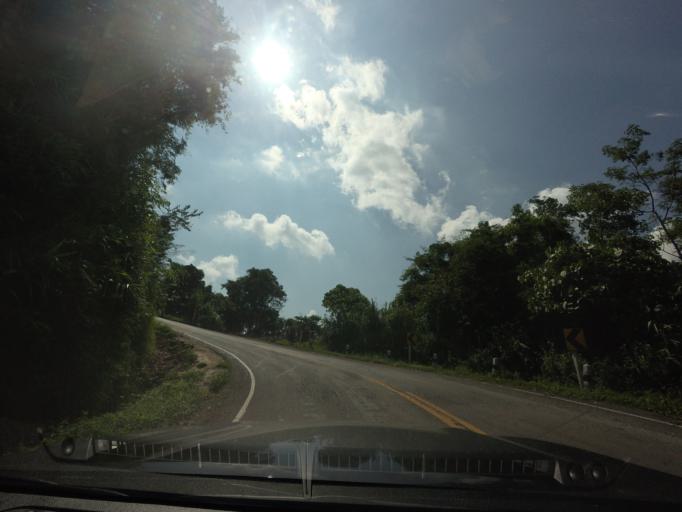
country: TH
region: Nan
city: Bo Kluea
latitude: 19.0661
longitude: 101.1181
